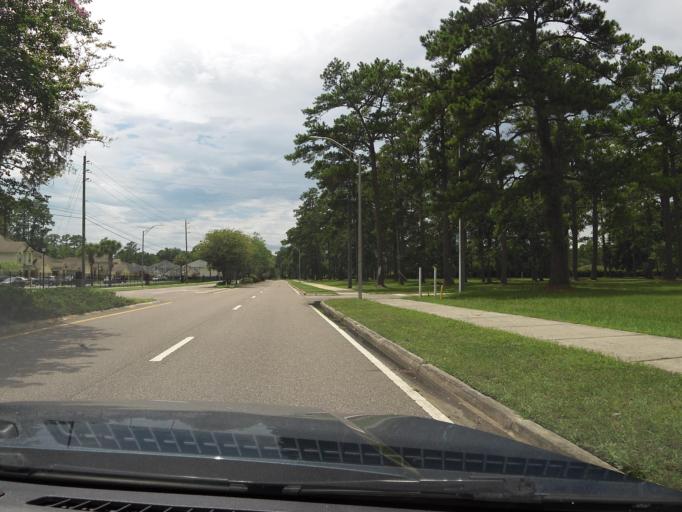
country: US
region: Florida
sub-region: Duval County
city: Jacksonville
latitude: 30.4274
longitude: -81.7212
